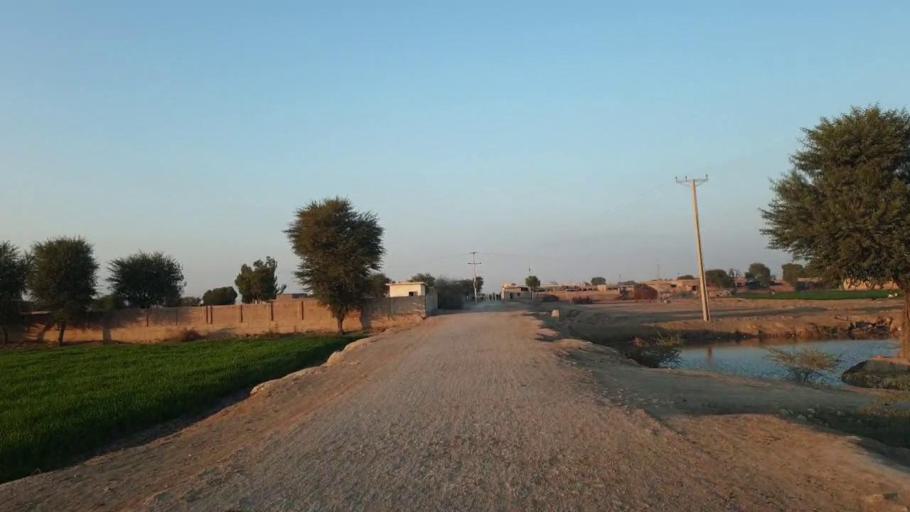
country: PK
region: Sindh
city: Shahpur Chakar
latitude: 26.1586
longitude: 68.5422
